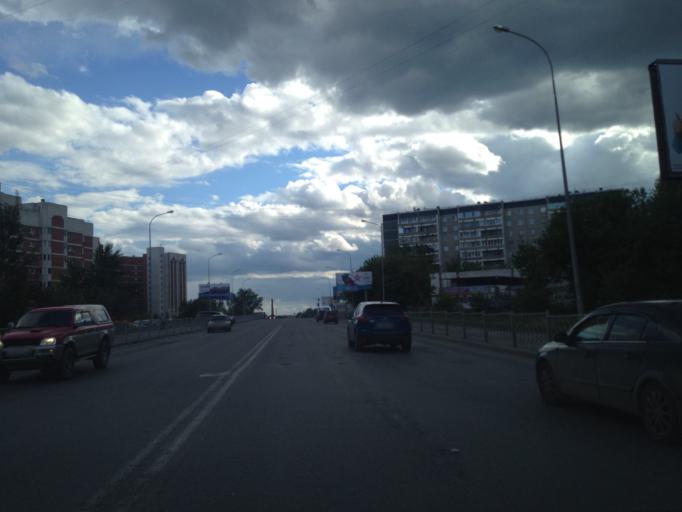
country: RU
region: Sverdlovsk
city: Yekaterinburg
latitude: 56.8512
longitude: 60.5694
